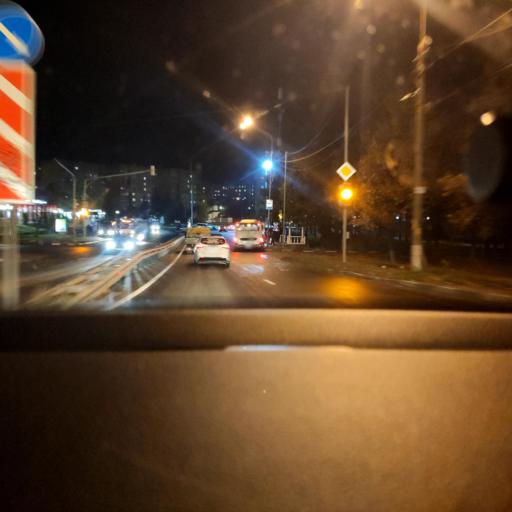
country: RU
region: Moskovskaya
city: Kotel'niki
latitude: 55.6319
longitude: 37.8475
